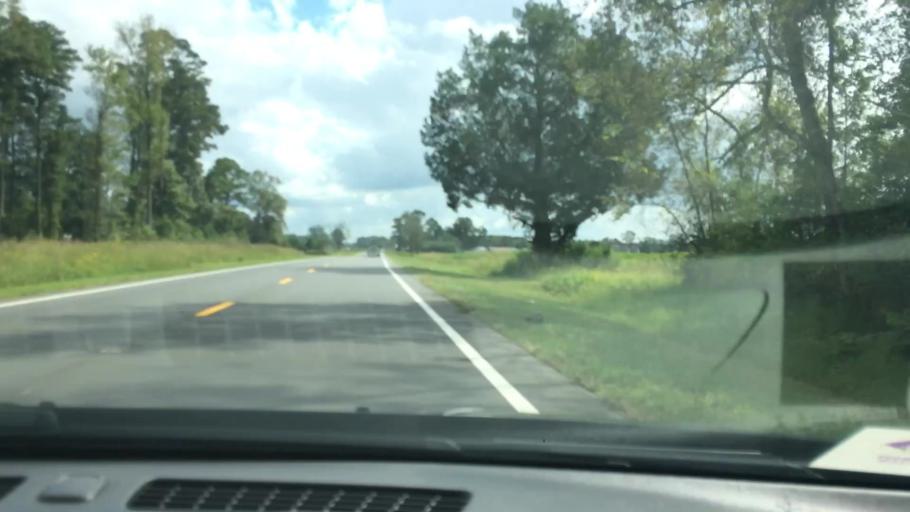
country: US
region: North Carolina
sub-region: Pitt County
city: Farmville
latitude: 35.5650
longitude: -77.5655
